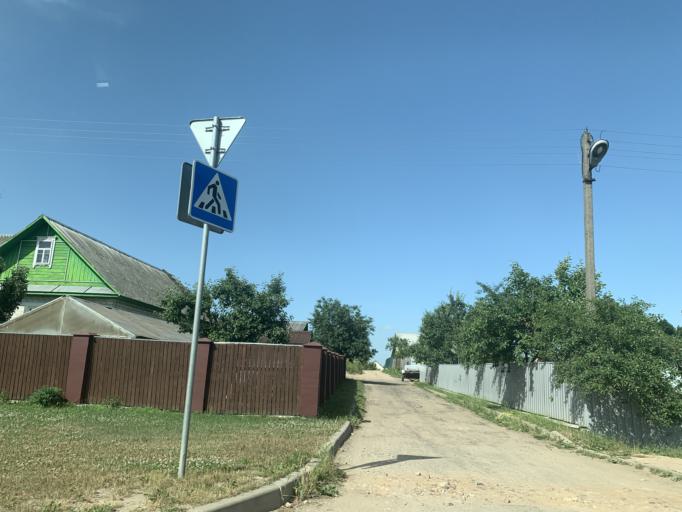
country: BY
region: Minsk
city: Dzyarzhynsk
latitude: 53.6970
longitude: 27.1064
